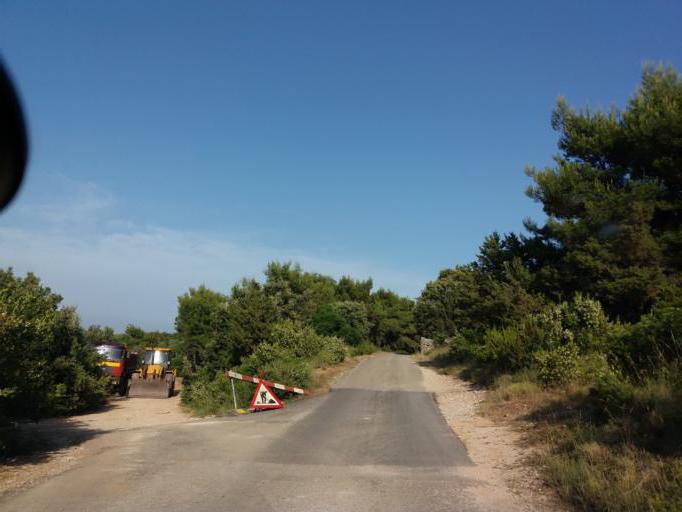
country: HR
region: Zadarska
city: Ugljan
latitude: 44.1422
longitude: 14.8446
